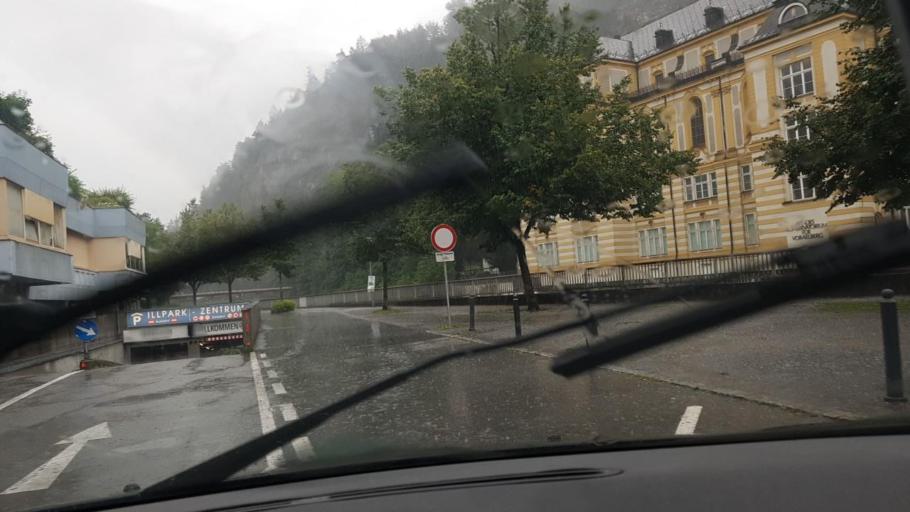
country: AT
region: Vorarlberg
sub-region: Politischer Bezirk Feldkirch
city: Feldkirch
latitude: 47.2355
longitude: 9.5963
